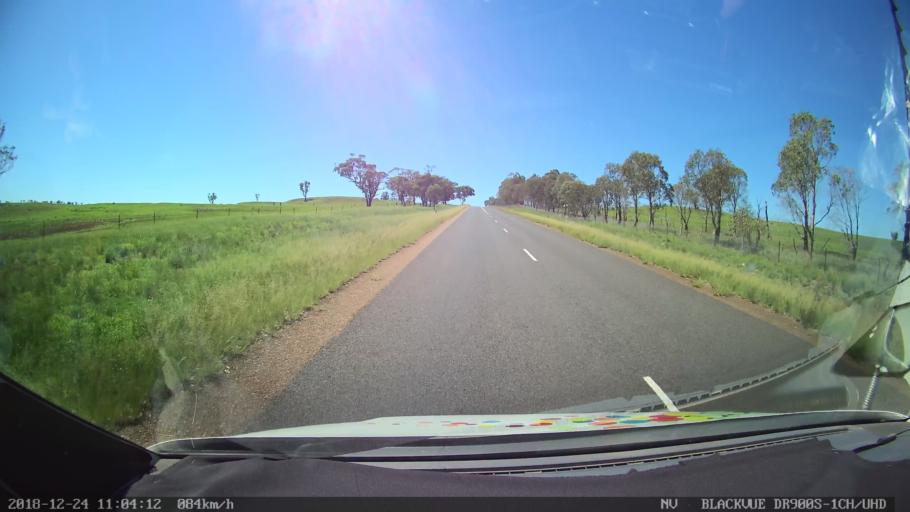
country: AU
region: New South Wales
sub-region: Upper Hunter Shire
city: Merriwa
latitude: -32.1062
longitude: 150.3709
